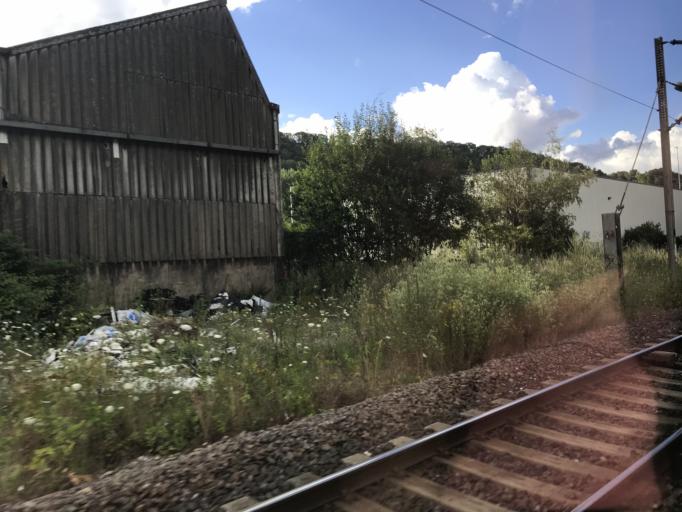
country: FR
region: Lorraine
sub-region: Departement de Meurthe-et-Moselle
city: Longwy
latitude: 49.5202
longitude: 5.7737
